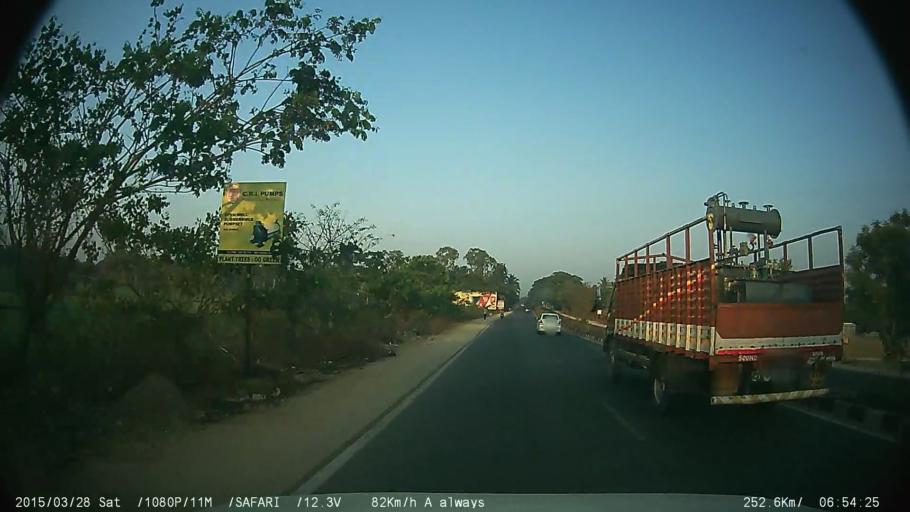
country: IN
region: Karnataka
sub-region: Mandya
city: Maddur
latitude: 12.5793
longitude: 77.0280
